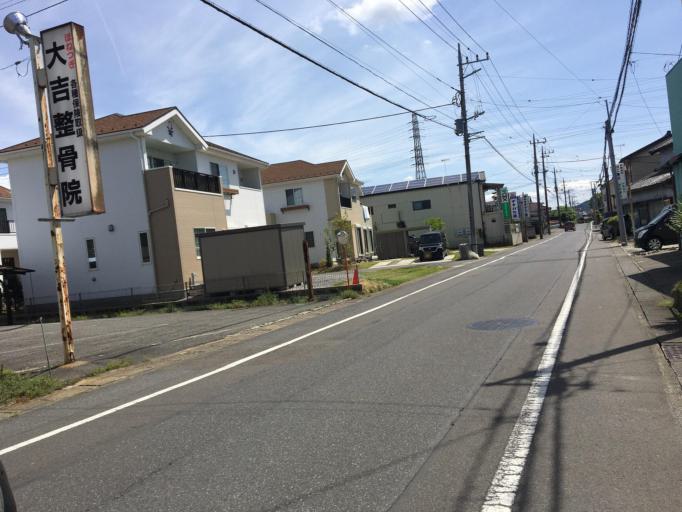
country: JP
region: Tochigi
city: Sano
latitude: 36.3156
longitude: 139.5631
